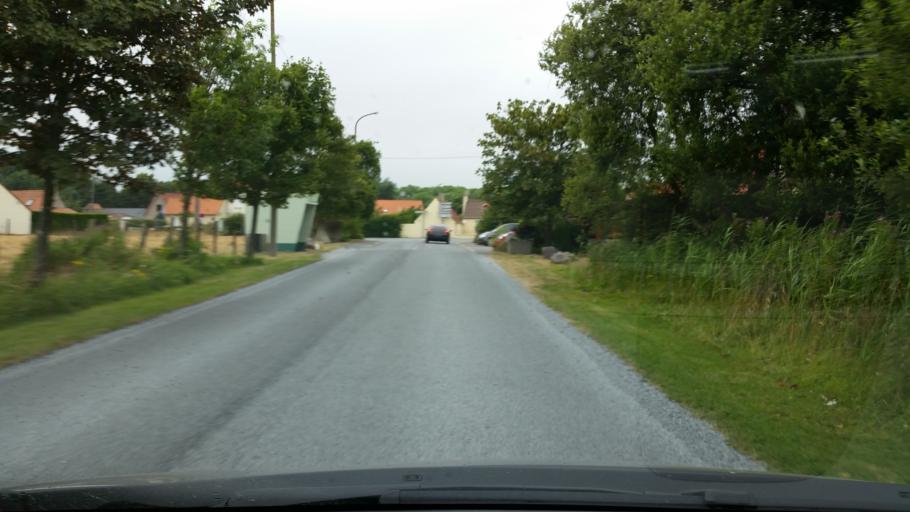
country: FR
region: Nord-Pas-de-Calais
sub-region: Departement du Pas-de-Calais
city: Marck
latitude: 50.9672
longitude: 1.9385
